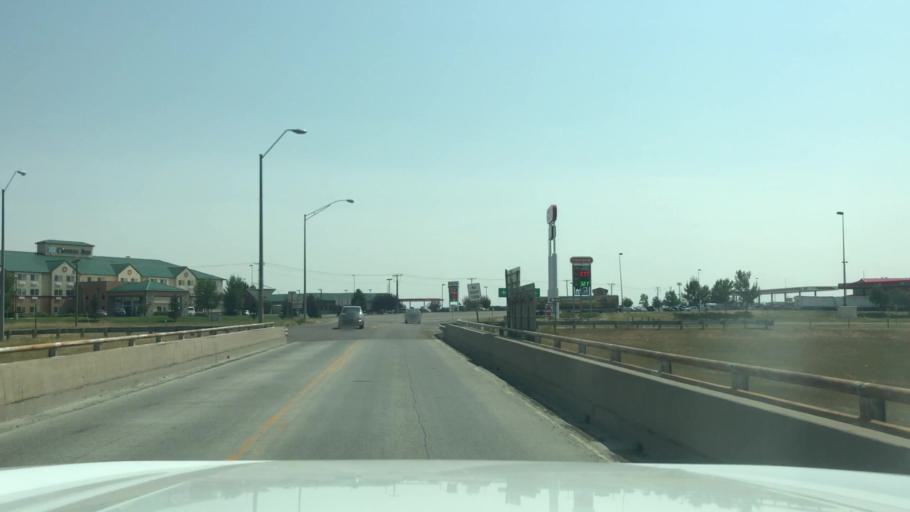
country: US
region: Montana
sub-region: Cascade County
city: Great Falls
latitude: 47.4724
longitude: -111.3611
